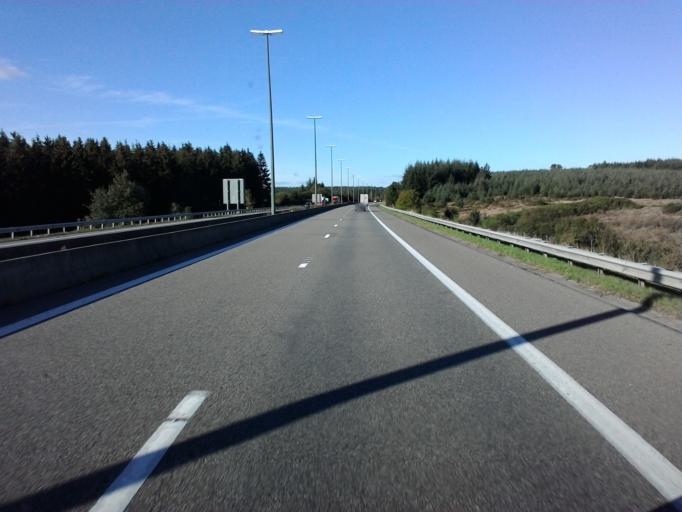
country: BE
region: Wallonia
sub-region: Province du Luxembourg
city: Bastogne
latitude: 50.0304
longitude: 5.7006
